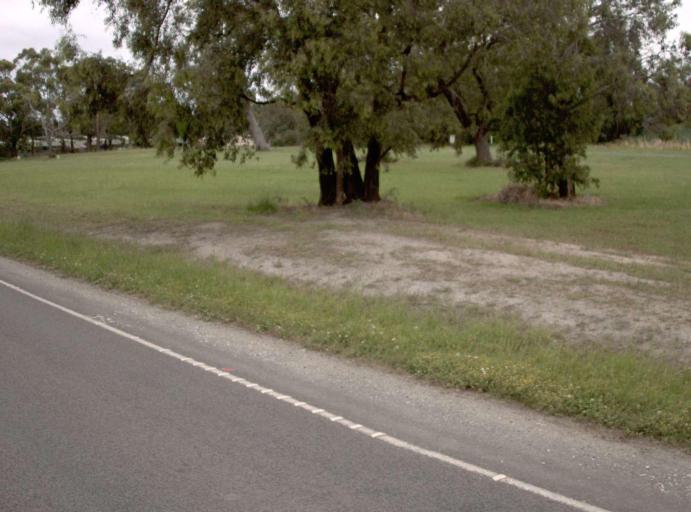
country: AU
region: Victoria
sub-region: Bass Coast
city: North Wonthaggi
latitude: -38.5318
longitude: 145.9515
